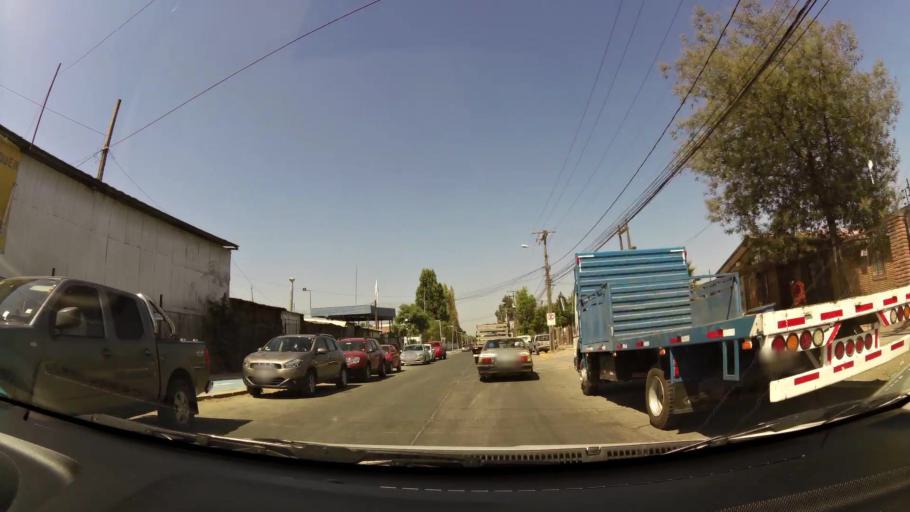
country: CL
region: Maule
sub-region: Provincia de Talca
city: Talca
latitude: -35.4204
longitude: -71.6360
